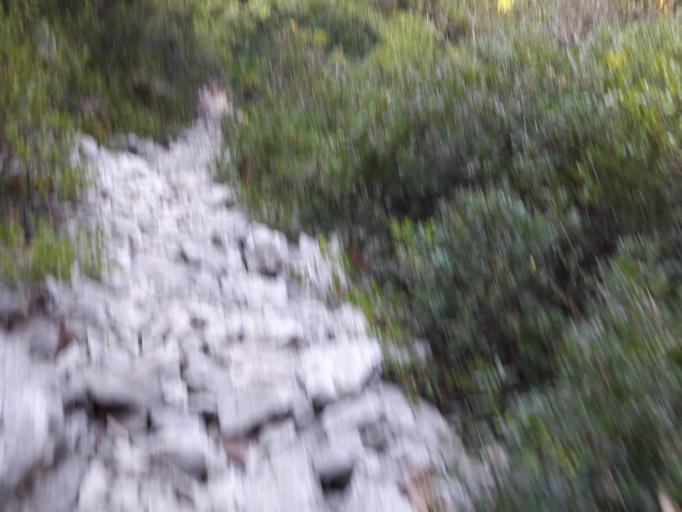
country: HR
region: Licko-Senjska
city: Novalja
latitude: 44.3635
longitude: 14.6931
